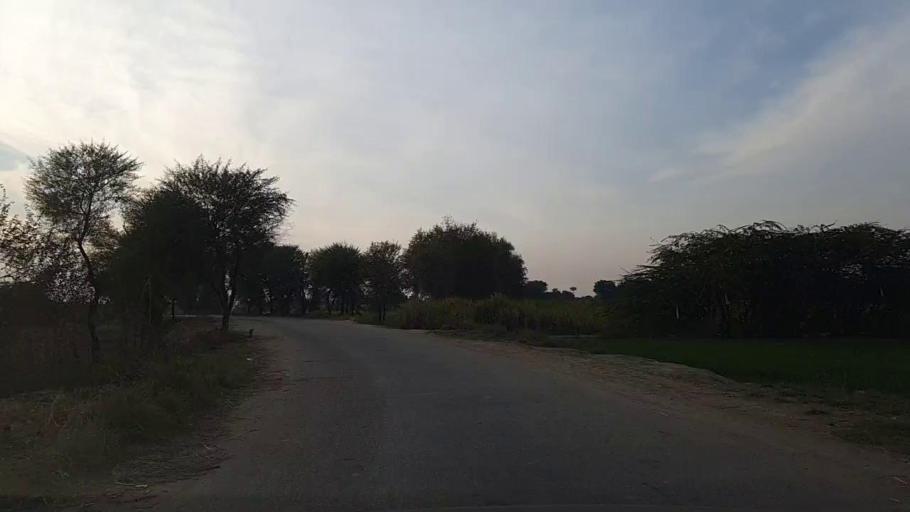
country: PK
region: Sindh
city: Daur
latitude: 26.4010
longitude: 68.4705
